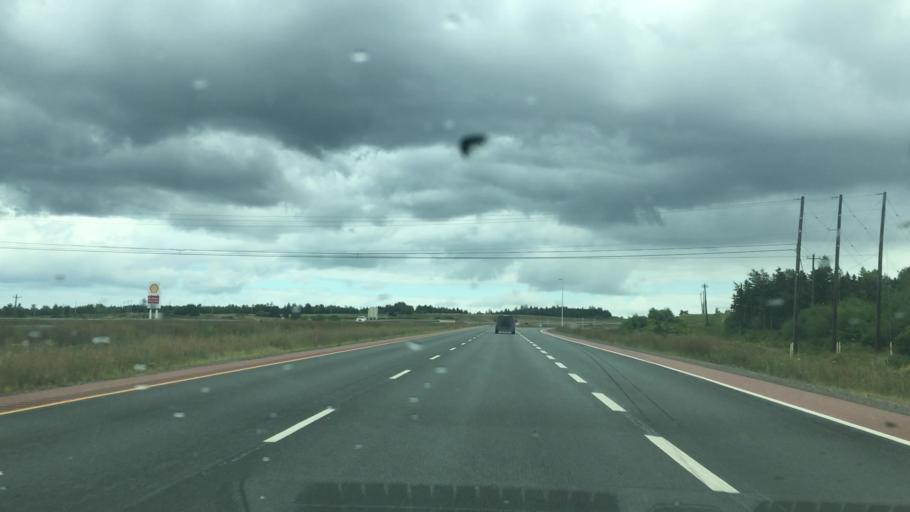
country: CA
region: Nova Scotia
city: Antigonish
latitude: 45.6093
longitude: -61.9748
